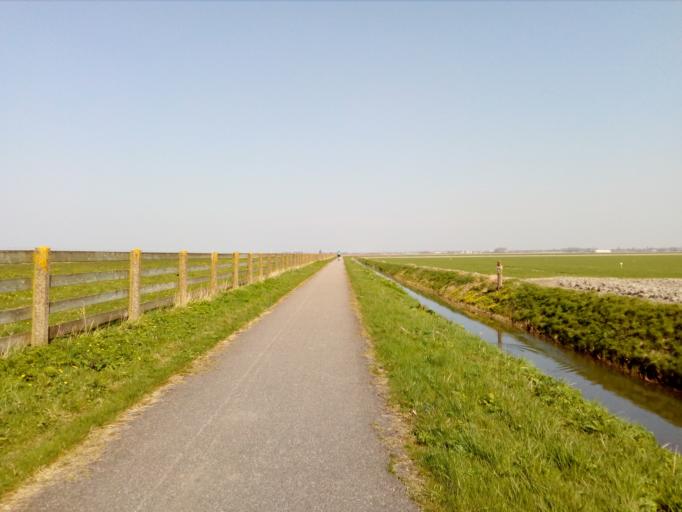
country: NL
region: South Holland
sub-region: Gemeente Waddinxveen
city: Groenswaard
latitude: 52.0536
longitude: 4.6062
